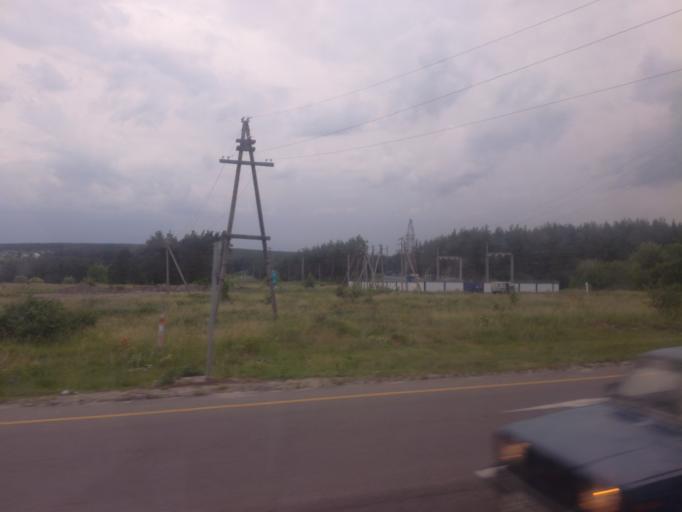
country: RU
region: Kursk
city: Voroshnevo
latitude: 51.7033
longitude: 36.0720
